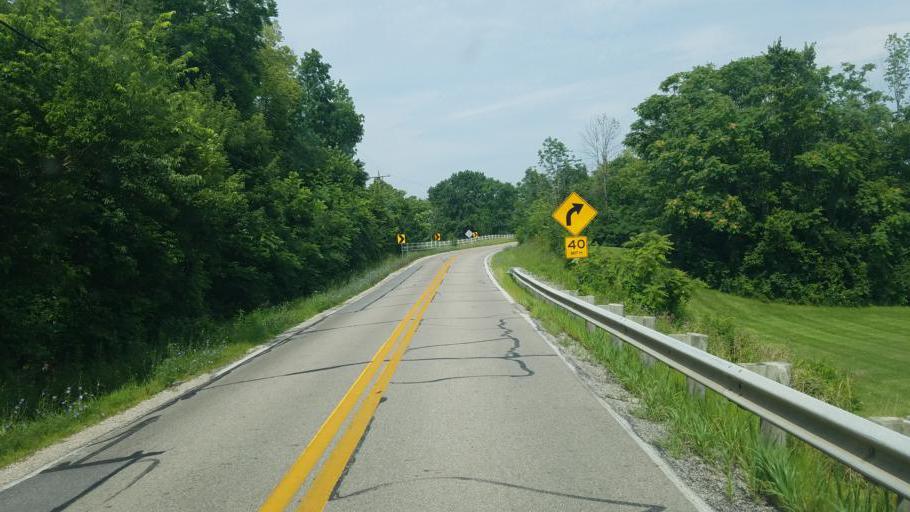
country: US
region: Ohio
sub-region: Franklin County
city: Lake Darby
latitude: 39.8925
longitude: -83.2260
